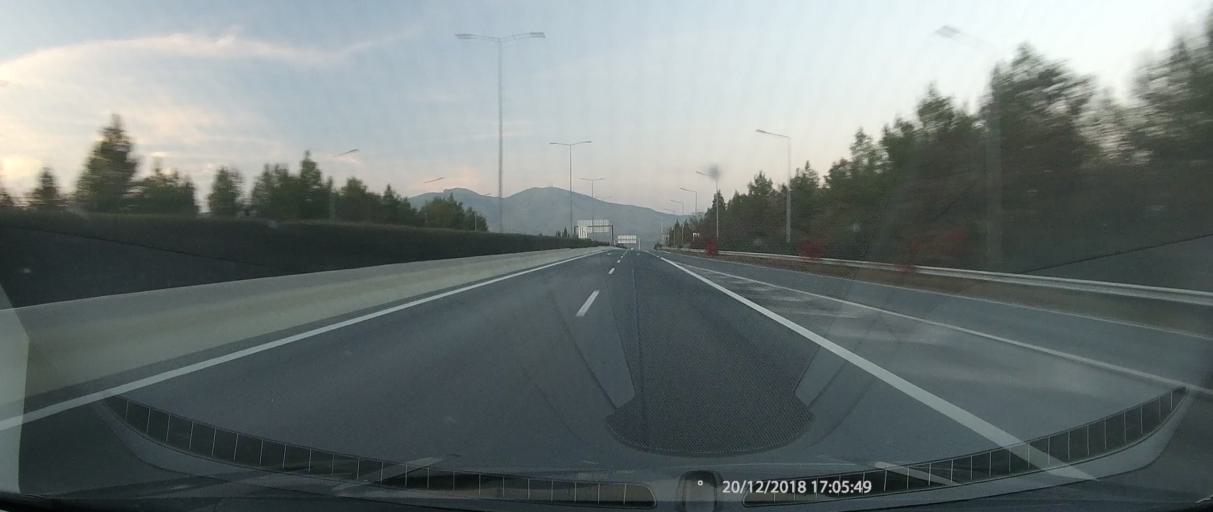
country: GR
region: Thessaly
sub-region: Nomos Larisis
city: Makrychori
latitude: 39.7472
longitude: 22.4753
